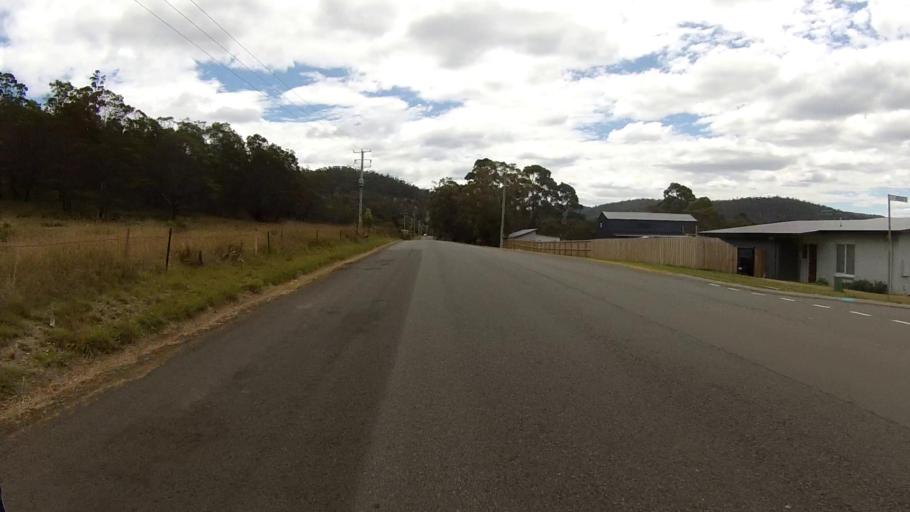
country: AU
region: Tasmania
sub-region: Sorell
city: Sorell
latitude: -42.5703
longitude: 147.8826
